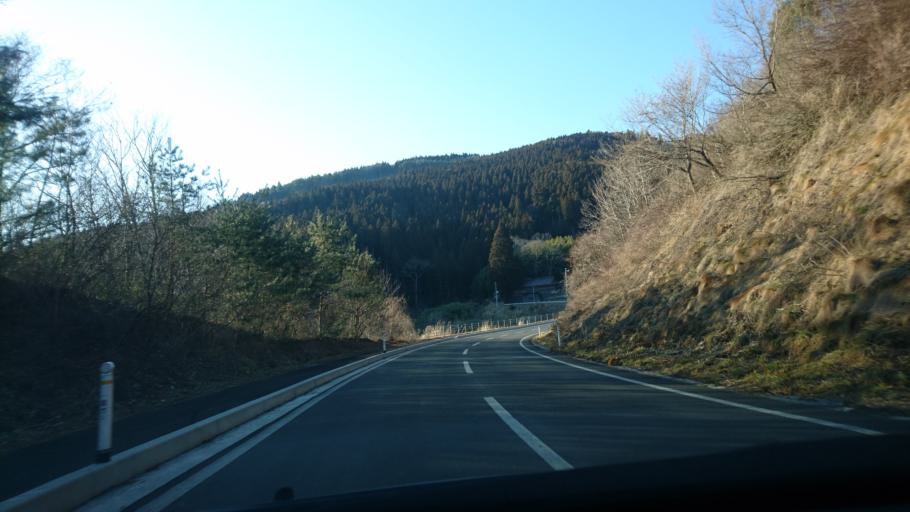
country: JP
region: Iwate
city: Ichinoseki
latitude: 38.8501
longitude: 141.3910
